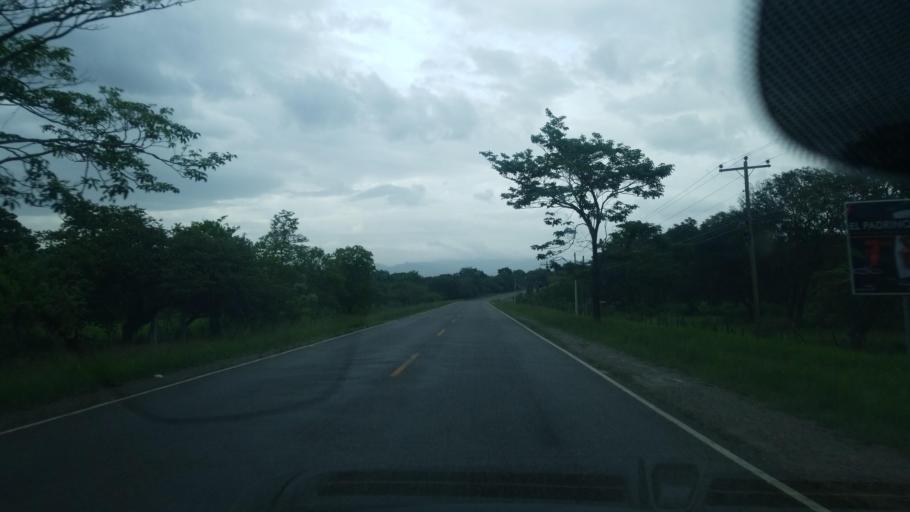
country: HN
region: Ocotepeque
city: Antigua Ocotepeque
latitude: 14.3833
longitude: -89.2077
